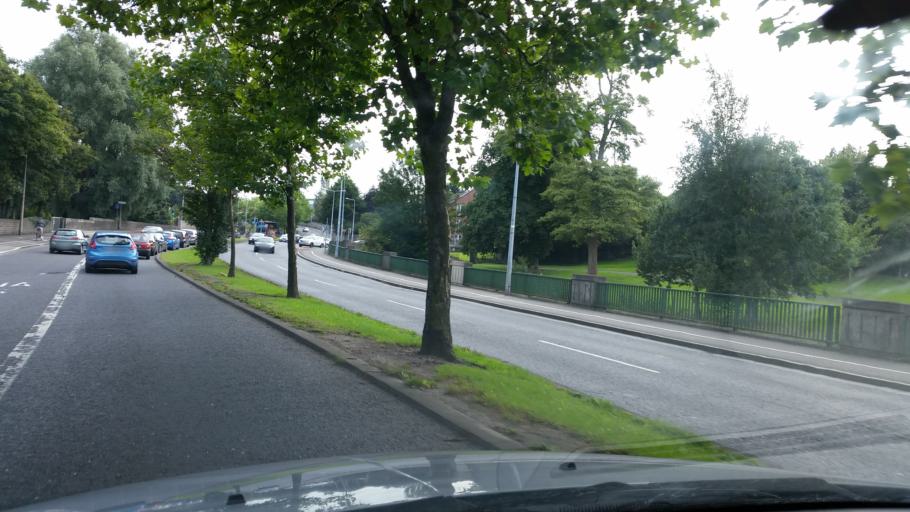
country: IE
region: Leinster
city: Cabra
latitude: 53.3769
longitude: -6.2870
